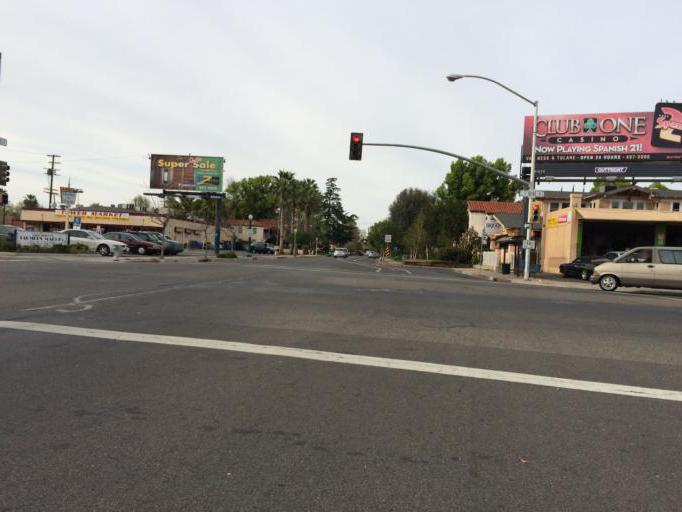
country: US
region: California
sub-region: Fresno County
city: Fresno
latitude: 36.7575
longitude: -119.7988
